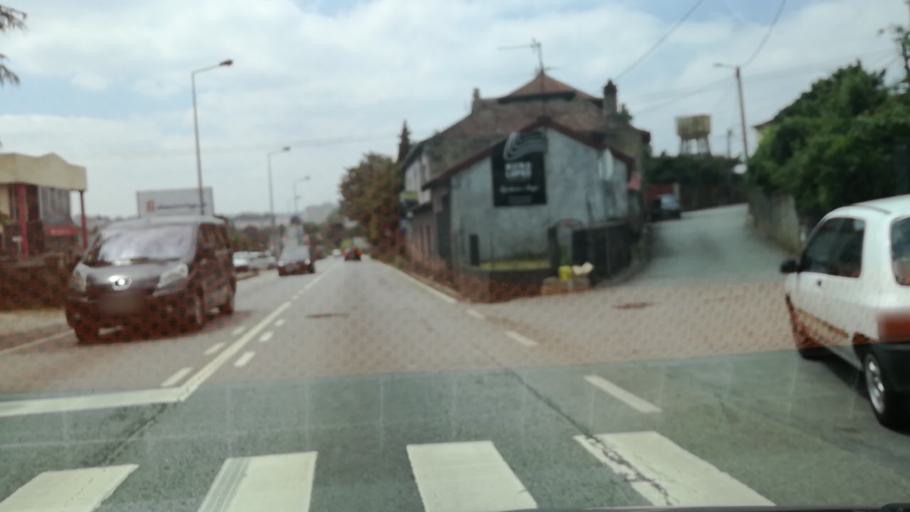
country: PT
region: Braga
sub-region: Vila Nova de Famalicao
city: Ferreiros
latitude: 41.3489
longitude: -8.5555
